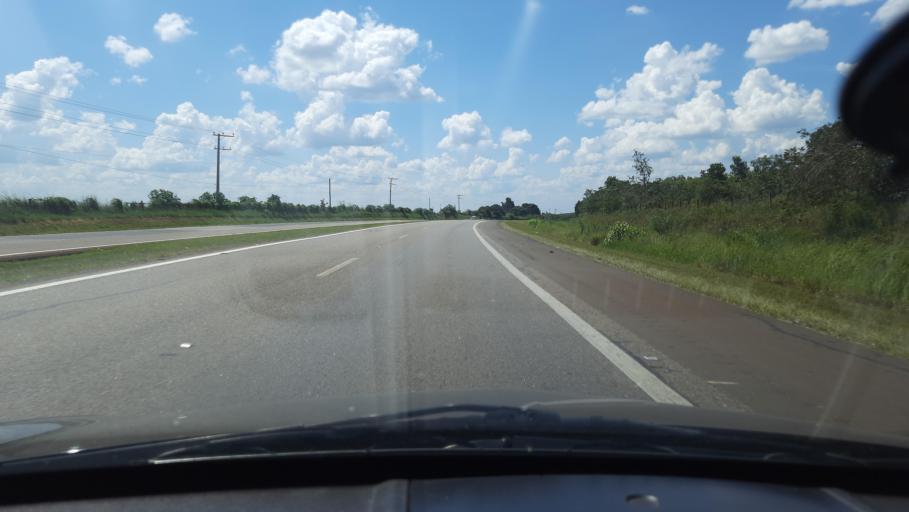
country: BR
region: Sao Paulo
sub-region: Casa Branca
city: Casa Branca
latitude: -21.7094
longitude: -47.0853
